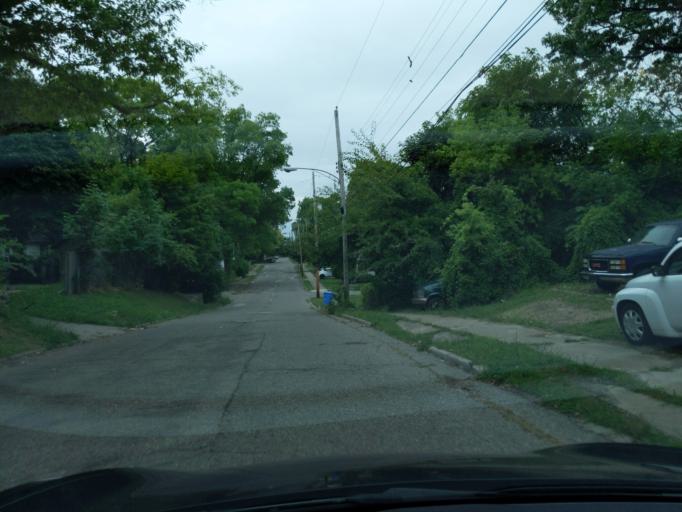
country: US
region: Michigan
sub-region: Ingham County
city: Lansing
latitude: 42.7225
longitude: -84.5290
